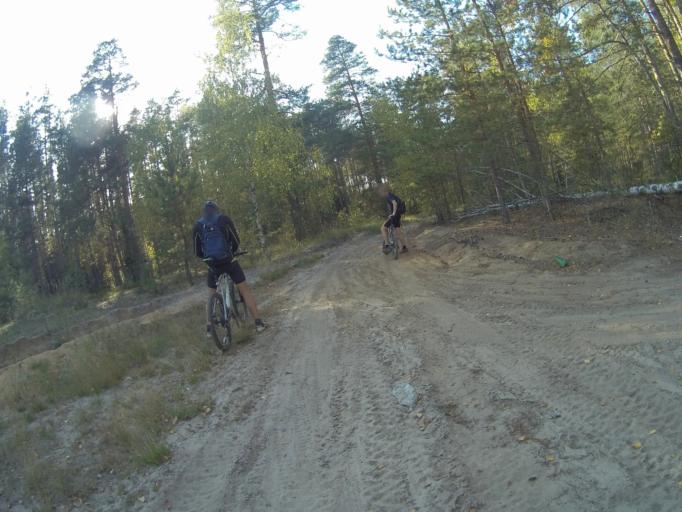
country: RU
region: Vladimir
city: Sobinka
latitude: 55.9225
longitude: 40.0672
